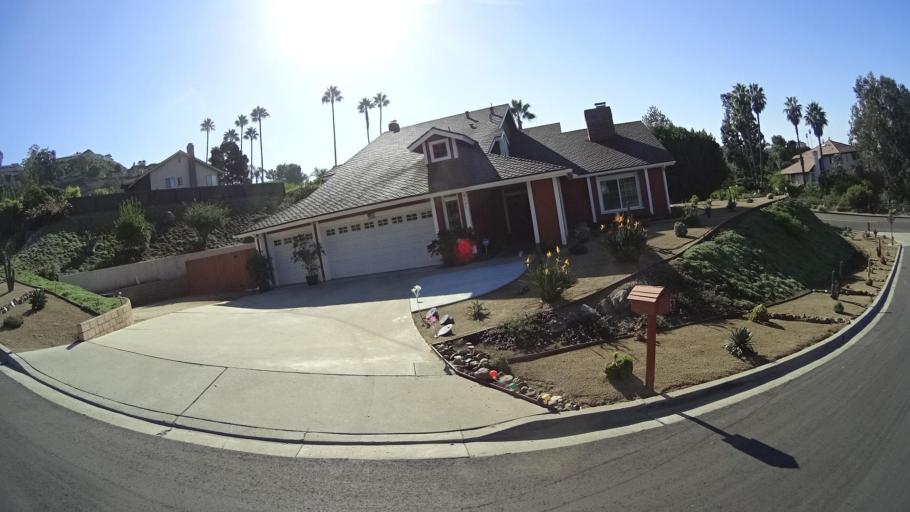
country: US
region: California
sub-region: San Diego County
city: Spring Valley
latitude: 32.7646
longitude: -116.9905
